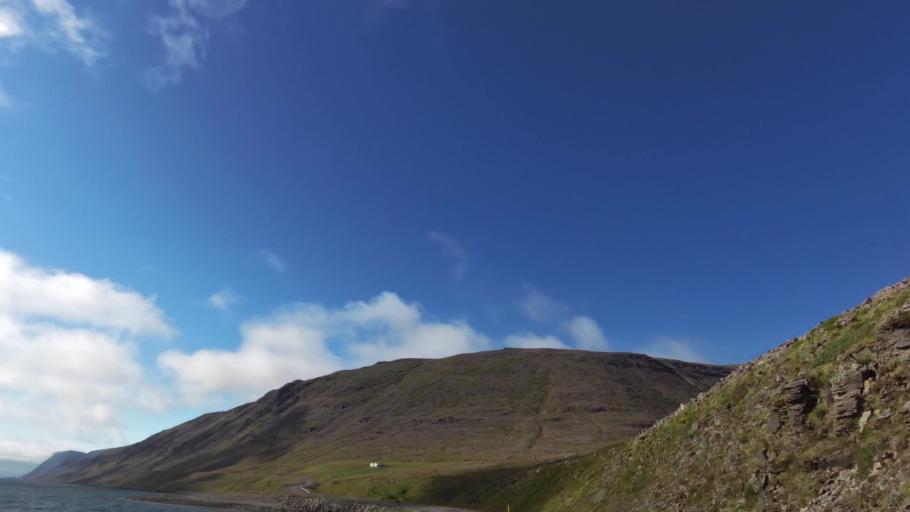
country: IS
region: West
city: Olafsvik
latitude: 65.5484
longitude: -23.8883
